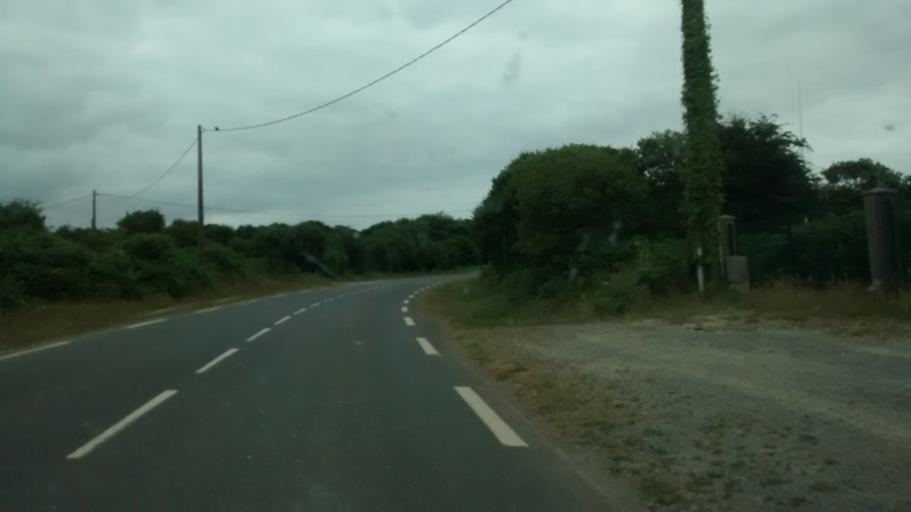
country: FR
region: Brittany
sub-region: Departement du Finistere
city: Plougastel-Daoulas
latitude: 48.3526
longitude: -4.4019
